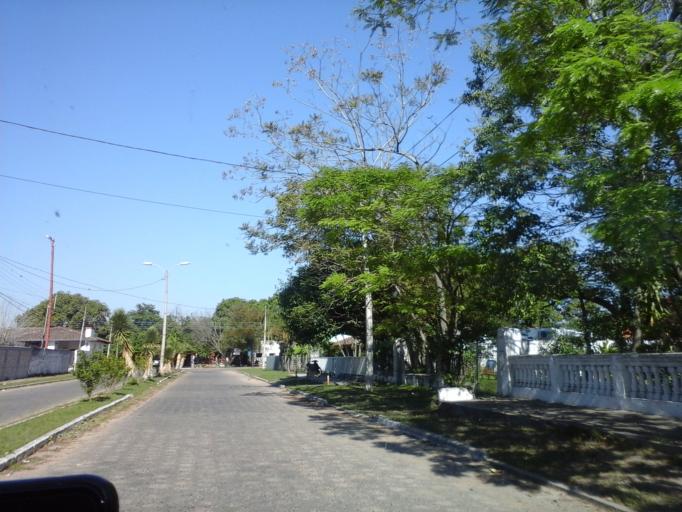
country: PY
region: Neembucu
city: Pilar
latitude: -26.8634
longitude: -58.3034
